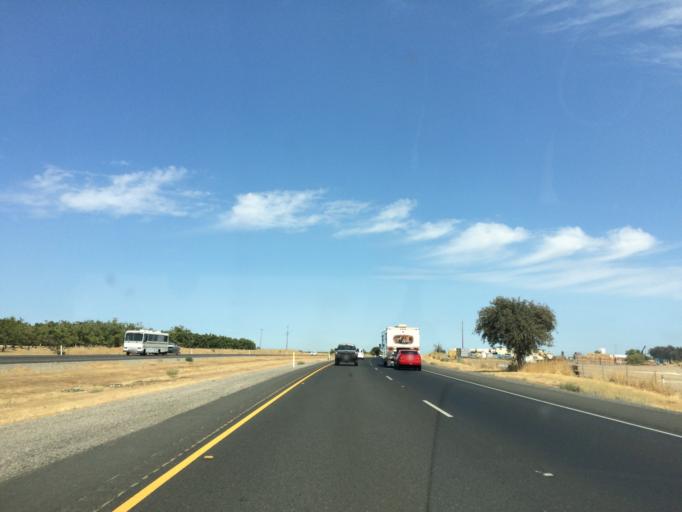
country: US
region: California
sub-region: Colusa County
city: Arbuckle
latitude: 38.9669
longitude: -122.0264
